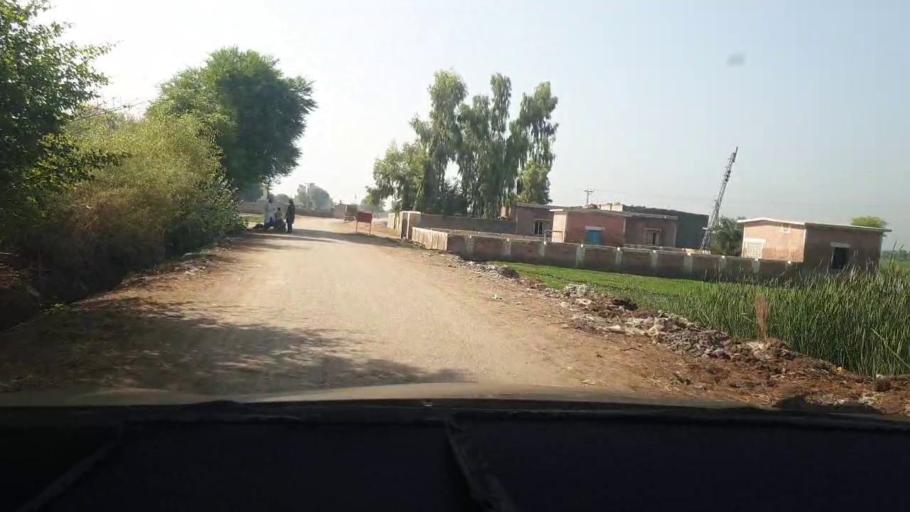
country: PK
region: Sindh
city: Kambar
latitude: 27.6034
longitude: 68.0930
